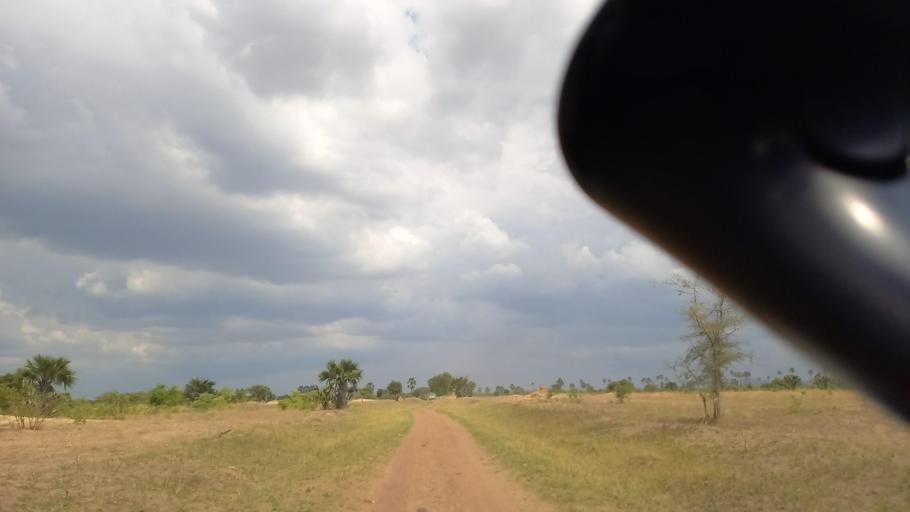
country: ZM
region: Lusaka
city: Kafue
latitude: -15.8301
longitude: 28.0619
